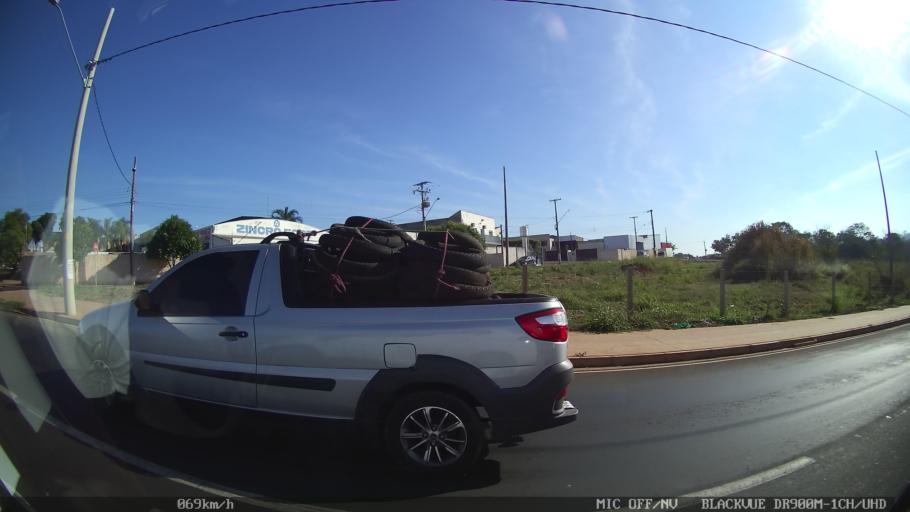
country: BR
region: Sao Paulo
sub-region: Sao Jose Do Rio Preto
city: Sao Jose do Rio Preto
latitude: -20.7631
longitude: -49.3770
